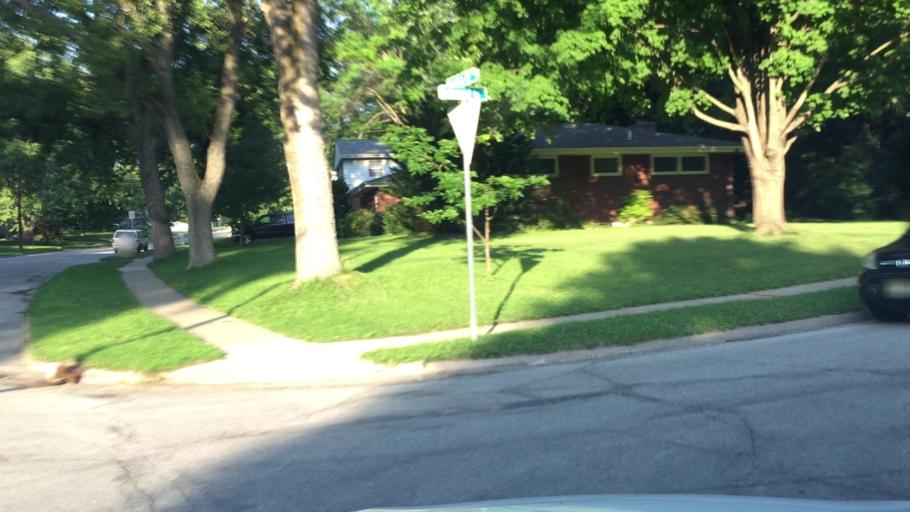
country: US
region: Iowa
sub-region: Johnson County
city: Iowa City
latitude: 41.6612
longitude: -91.5080
